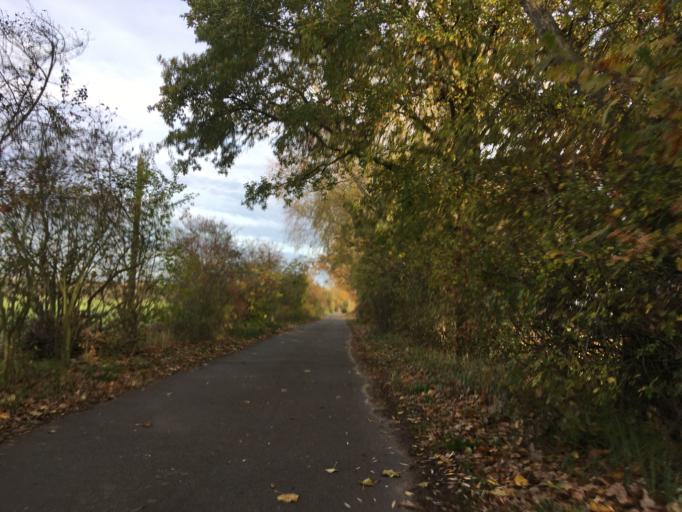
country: DE
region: Brandenburg
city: Luebben
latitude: 51.9794
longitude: 13.8741
